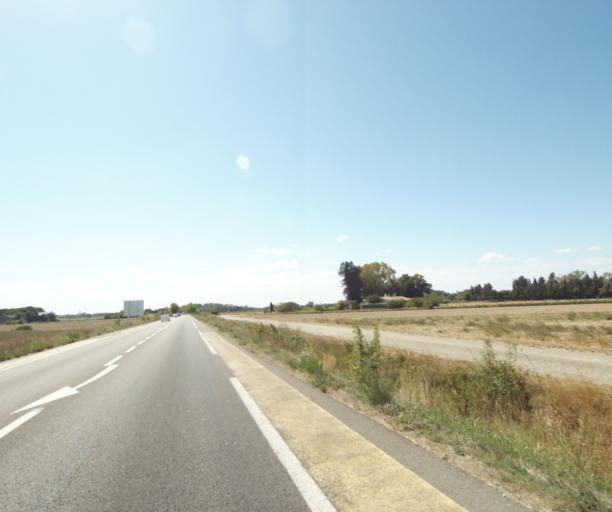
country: FR
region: Languedoc-Roussillon
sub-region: Departement du Gard
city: Rodilhan
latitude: 43.8318
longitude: 4.4246
